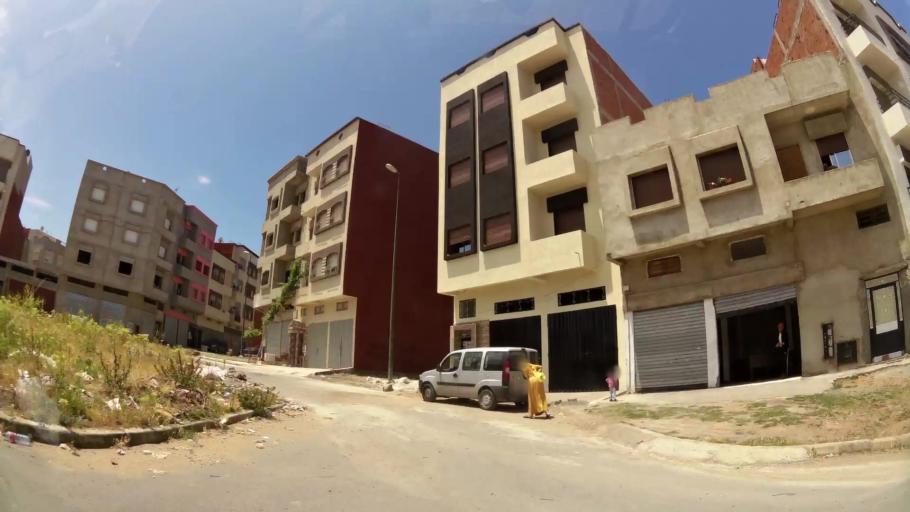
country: MA
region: Gharb-Chrarda-Beni Hssen
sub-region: Kenitra Province
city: Kenitra
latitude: 34.2714
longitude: -6.6182
